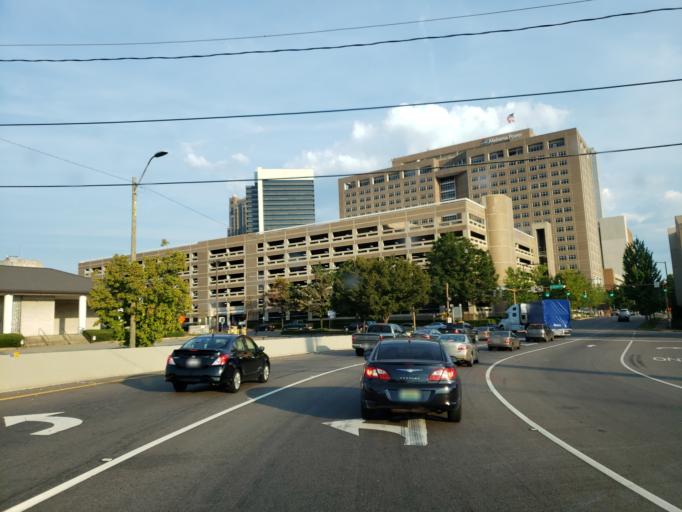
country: US
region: Alabama
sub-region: Jefferson County
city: Birmingham
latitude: 33.5201
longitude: -86.8152
